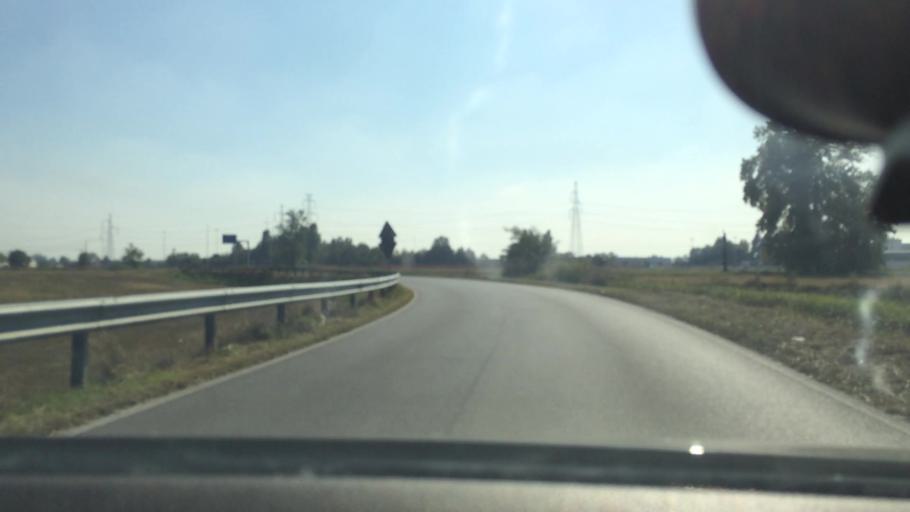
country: IT
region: Lombardy
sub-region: Citta metropolitana di Milano
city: Casate
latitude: 45.4884
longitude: 8.8287
